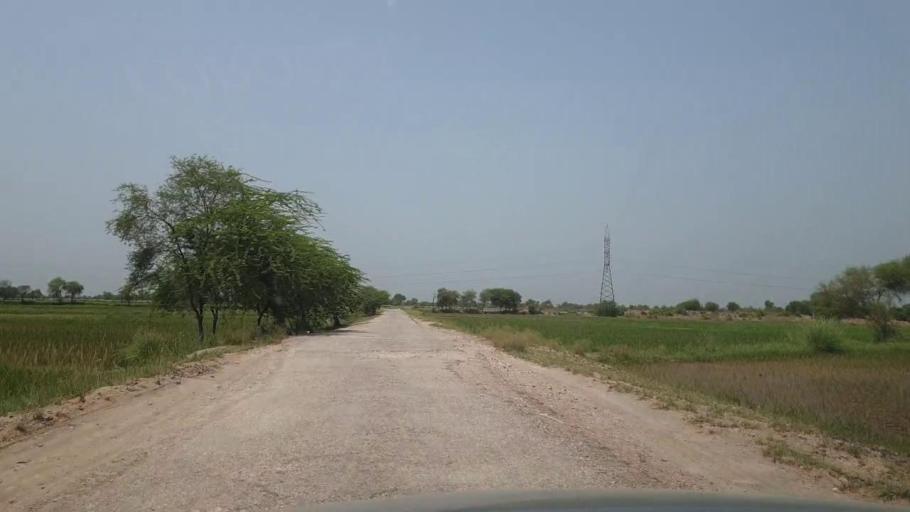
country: PK
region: Sindh
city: Garhi Yasin
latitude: 27.8721
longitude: 68.4489
